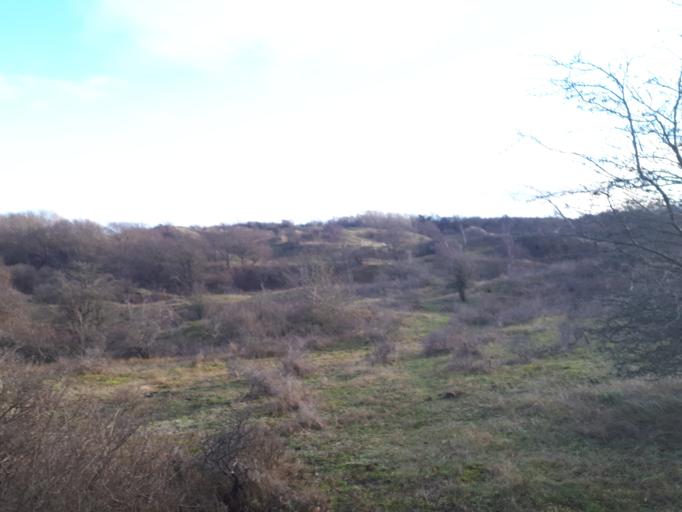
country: NL
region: South Holland
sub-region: Gemeente Wassenaar
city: Wassenaar
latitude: 52.1395
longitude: 4.3619
